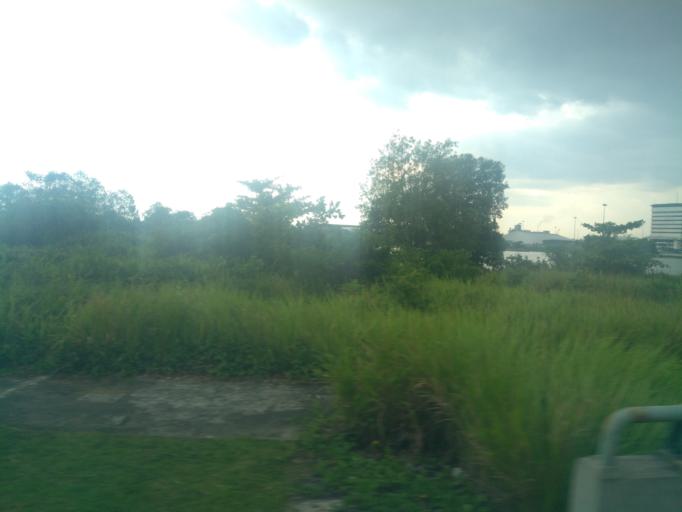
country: MY
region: Sarawak
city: Kuching
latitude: 1.5593
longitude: 110.3977
